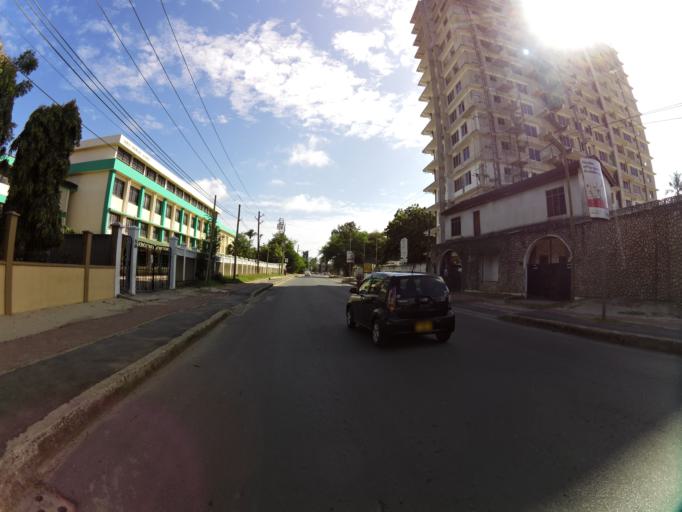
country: TZ
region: Dar es Salaam
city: Dar es Salaam
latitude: -6.7985
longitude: 39.2797
